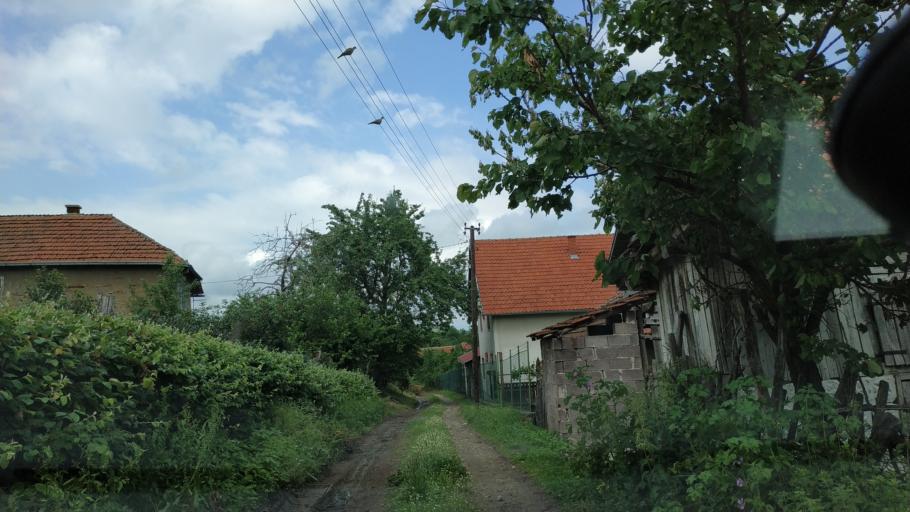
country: RS
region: Central Serbia
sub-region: Nisavski Okrug
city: Aleksinac
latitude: 43.4261
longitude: 21.5799
